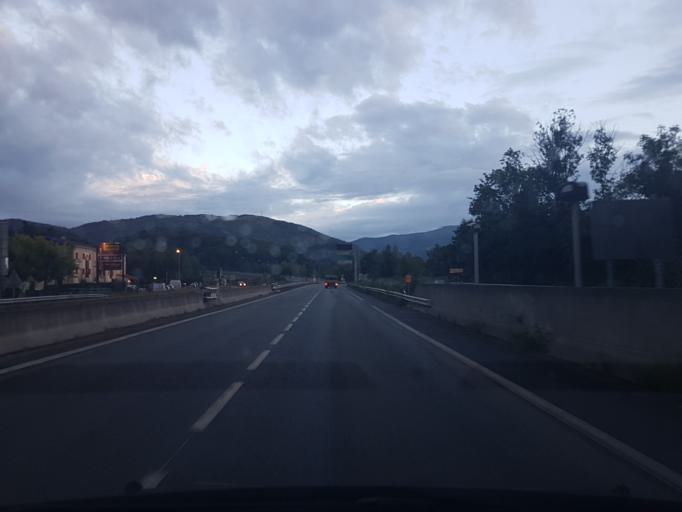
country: FR
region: Midi-Pyrenees
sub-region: Departement de l'Ariege
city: Varilhes
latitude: 43.0070
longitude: 1.6140
